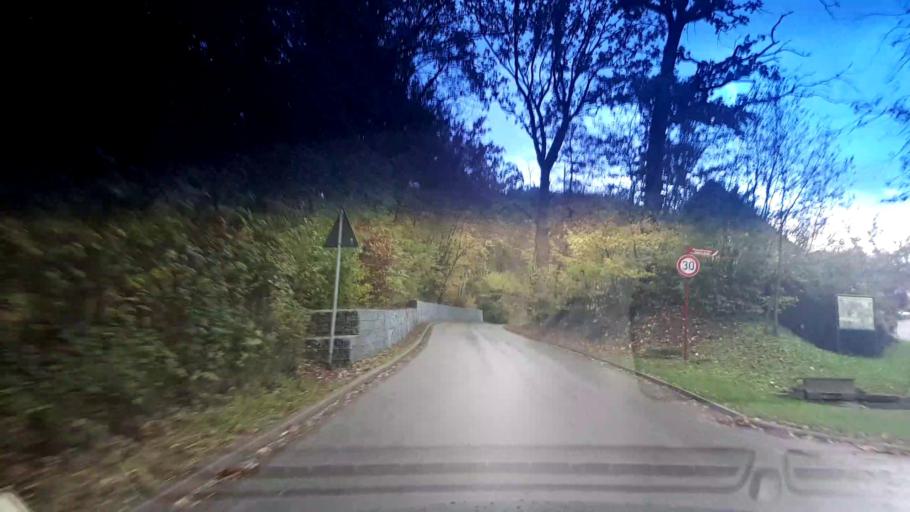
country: DE
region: Bavaria
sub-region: Upper Franconia
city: Viereth-Trunstadt
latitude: 49.9197
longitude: 10.7771
